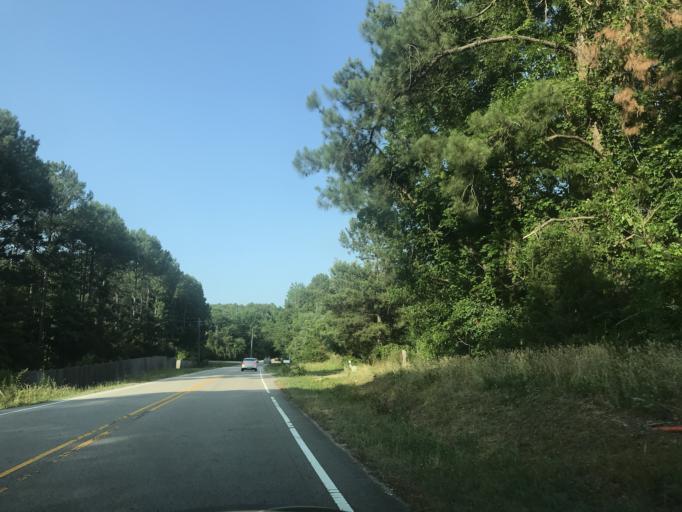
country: US
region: North Carolina
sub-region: Wake County
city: Rolesville
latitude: 35.8604
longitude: -78.4932
